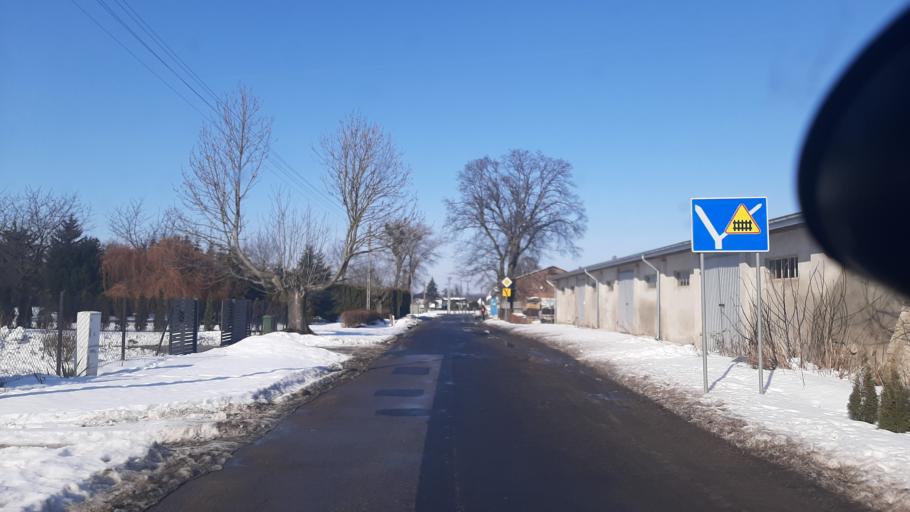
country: PL
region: Lublin Voivodeship
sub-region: Powiat lubelski
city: Wojciechow
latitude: 51.2870
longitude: 22.2820
